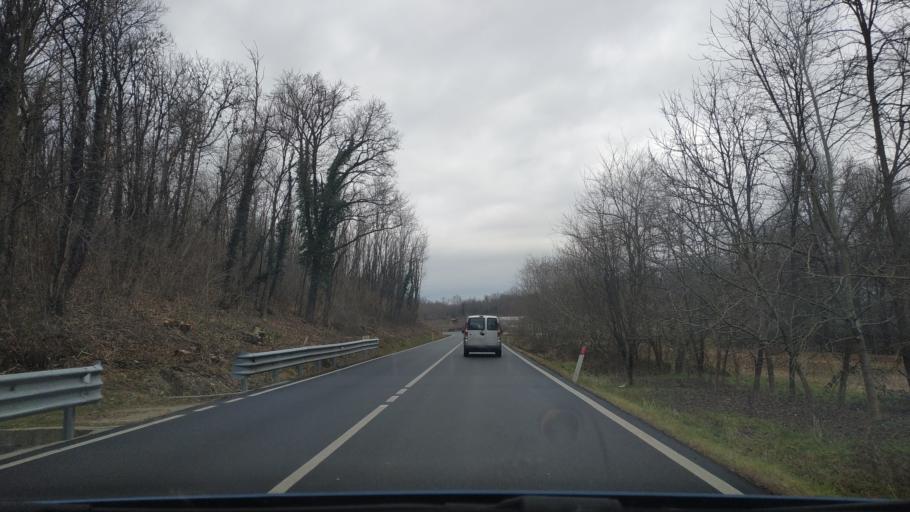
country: IT
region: Piedmont
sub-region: Provincia di Torino
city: Candia Canavese
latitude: 45.3441
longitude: 7.8859
